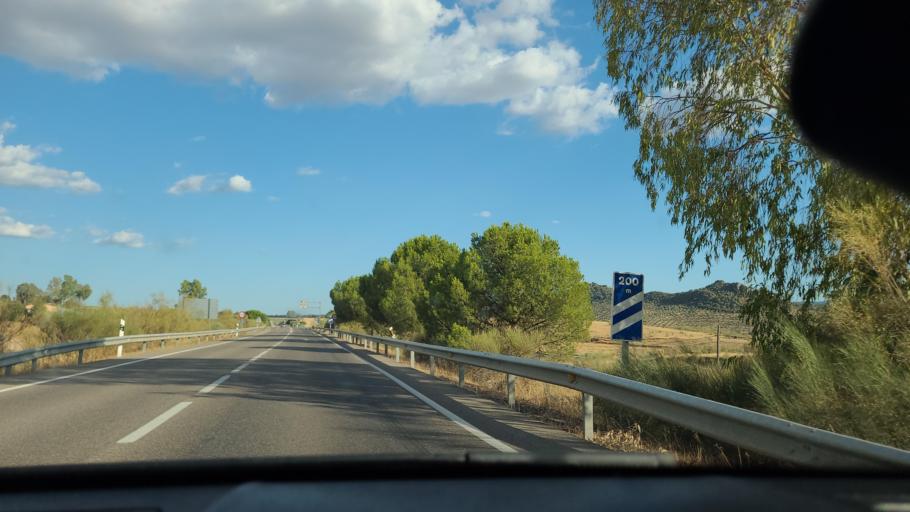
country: ES
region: Andalusia
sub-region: Province of Cordoba
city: Belmez
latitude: 38.2676
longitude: -5.1882
